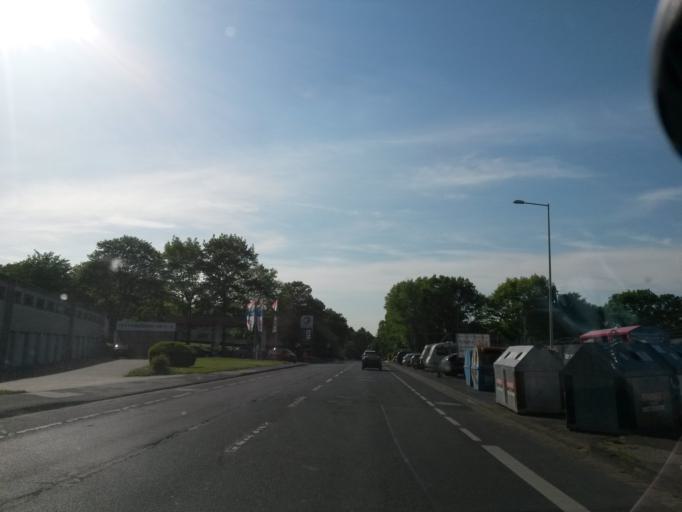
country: DE
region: North Rhine-Westphalia
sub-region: Regierungsbezirk Koln
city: Alfter
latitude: 50.7093
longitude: 7.0559
